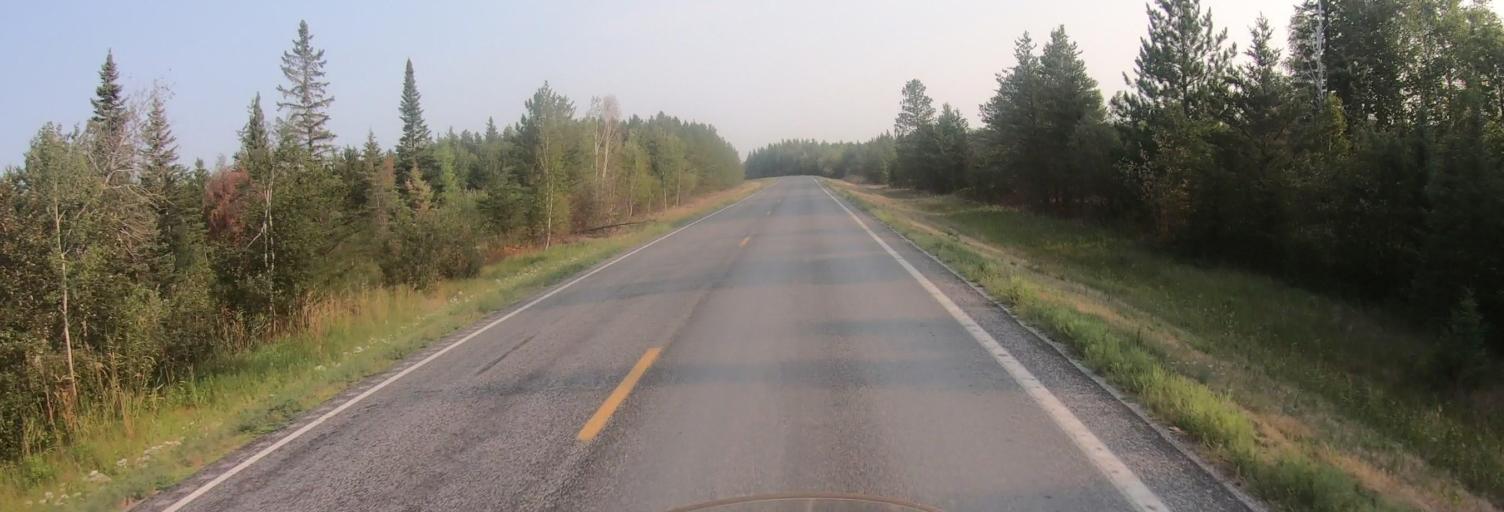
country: US
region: Minnesota
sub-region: Roseau County
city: Warroad
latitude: 48.7353
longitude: -95.3303
